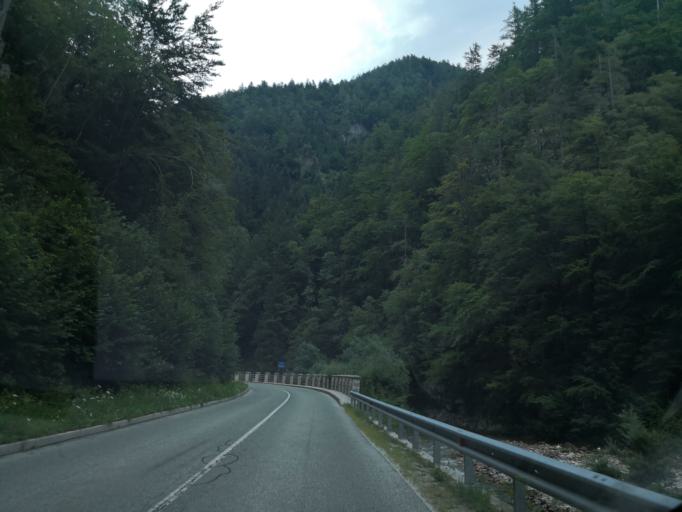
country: SI
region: Jezersko
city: Zgornje Jezersko
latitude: 46.3457
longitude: 14.4810
